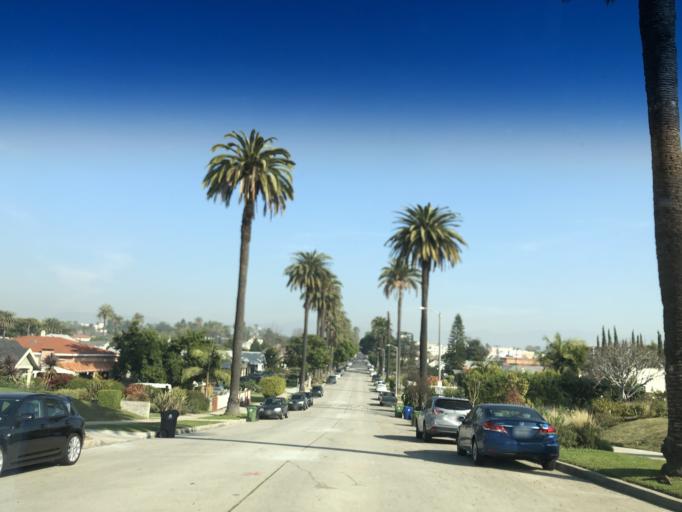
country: US
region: California
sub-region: Los Angeles County
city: Hollywood
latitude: 34.0512
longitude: -118.3264
